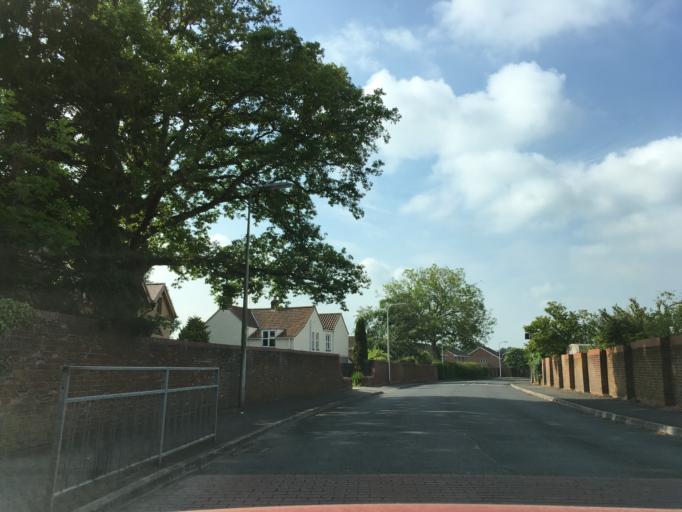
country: GB
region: England
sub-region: North Somerset
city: Nailsea
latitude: 51.4323
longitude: -2.7435
